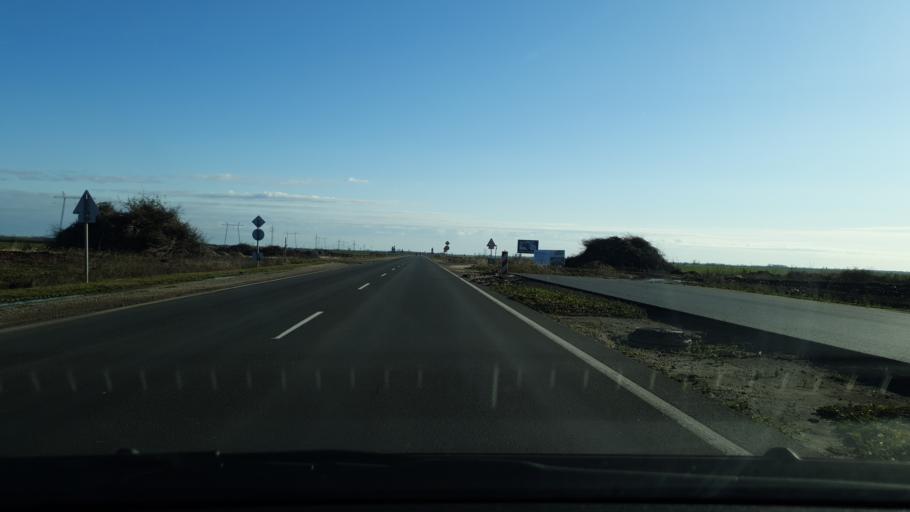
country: HU
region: Pest
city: Abony
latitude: 47.2158
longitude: 20.0424
